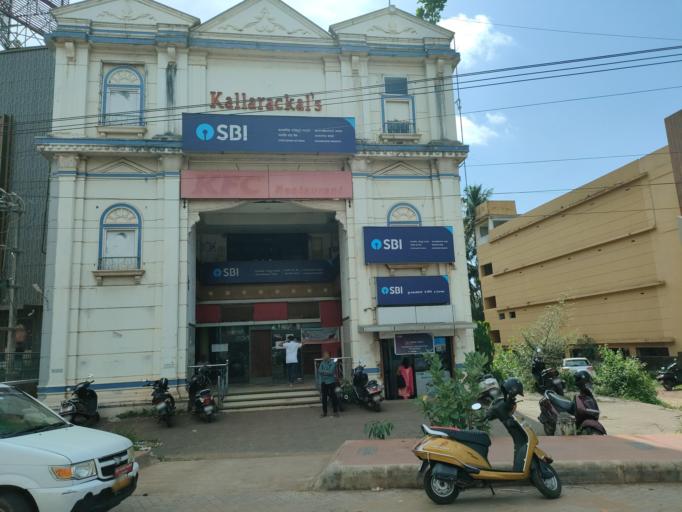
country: IN
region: Kerala
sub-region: Kasaragod District
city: Kasaragod
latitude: 12.5047
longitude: 74.9935
